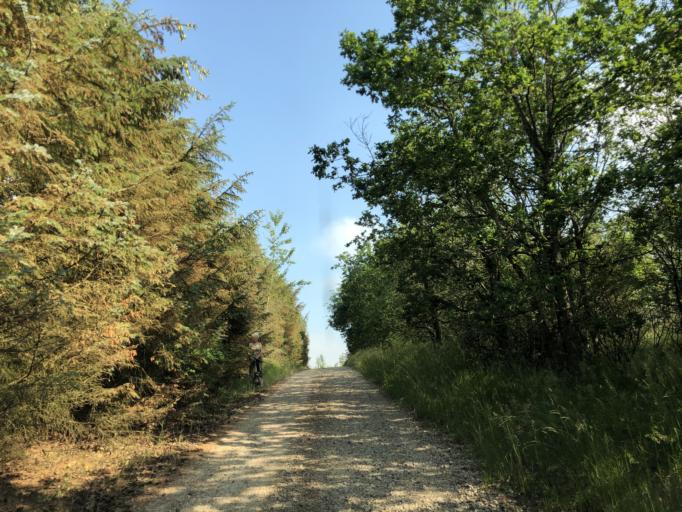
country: DK
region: Central Jutland
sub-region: Ringkobing-Skjern Kommune
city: Videbaek
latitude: 56.1546
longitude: 8.5220
